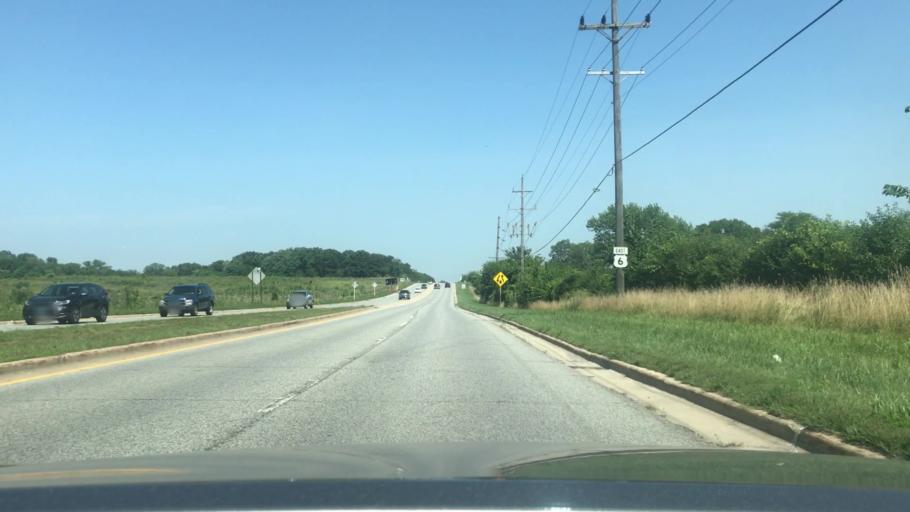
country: US
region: Illinois
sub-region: Cook County
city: Oak Forest
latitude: 41.6033
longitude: -87.7316
